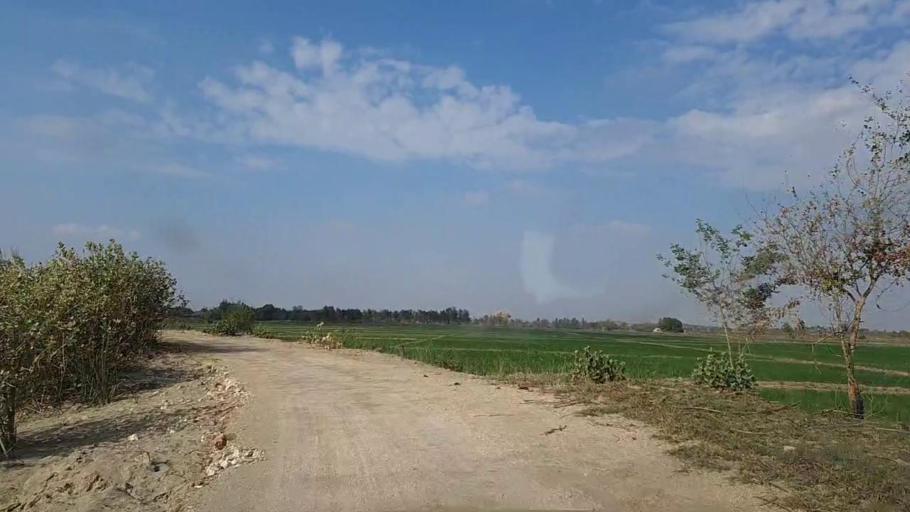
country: PK
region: Sindh
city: Sanghar
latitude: 26.2722
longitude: 69.0121
